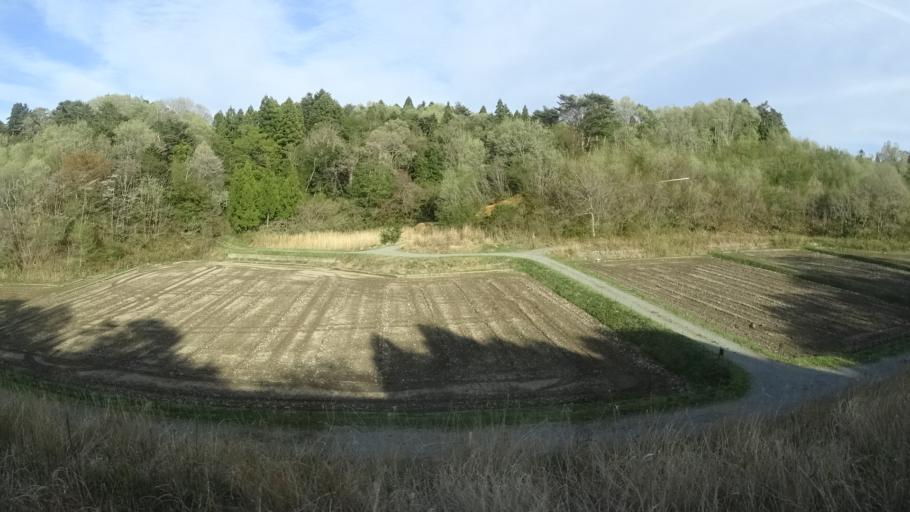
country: JP
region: Fukushima
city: Namie
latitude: 37.5227
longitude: 140.9767
